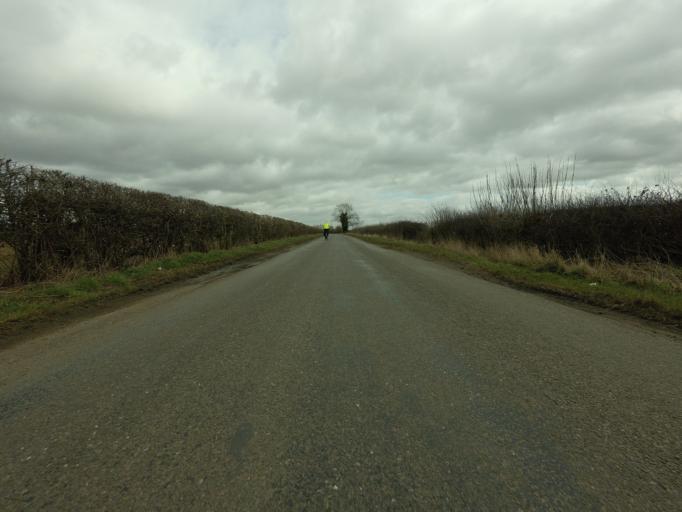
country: GB
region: England
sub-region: Lincolnshire
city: Barrowby
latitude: 52.8732
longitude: -0.6769
